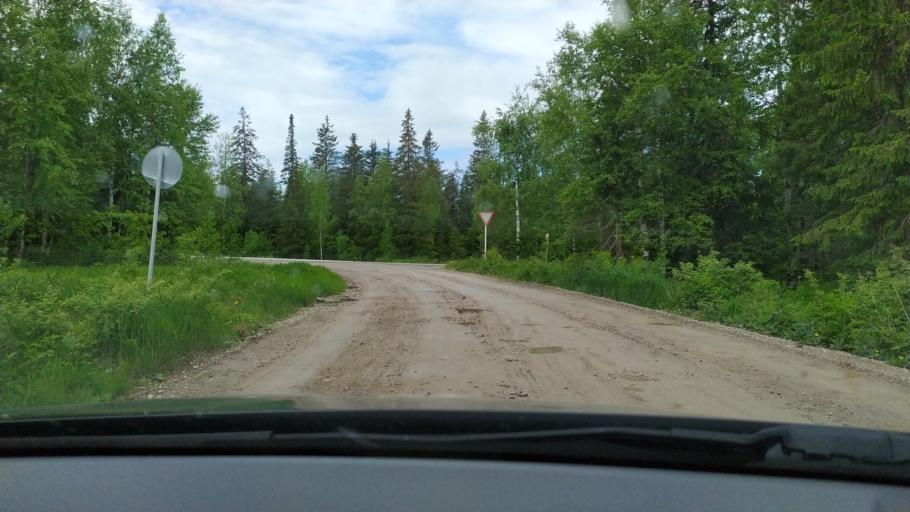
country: RU
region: Perm
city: Gremyachinsk
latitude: 58.5109
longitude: 57.8128
